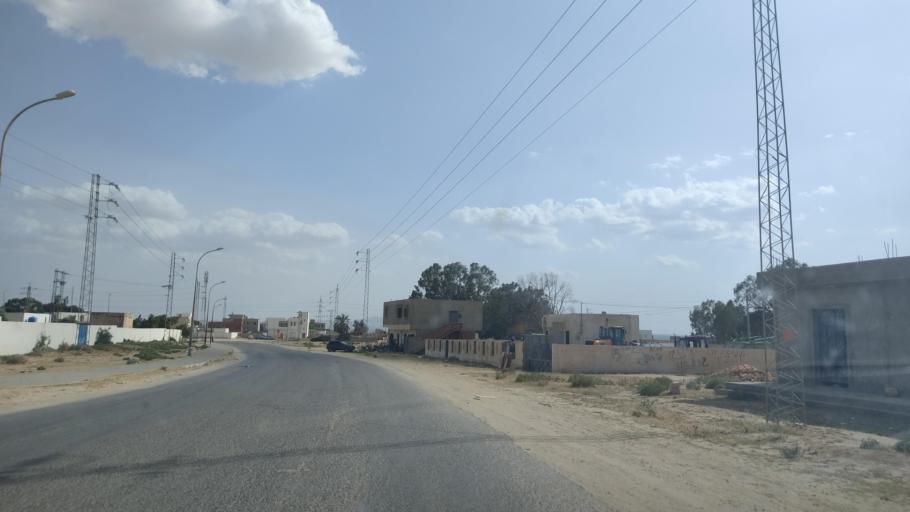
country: TN
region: Sidi Bu Zayd
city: Sidi Bouzid
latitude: 35.1019
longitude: 9.5345
